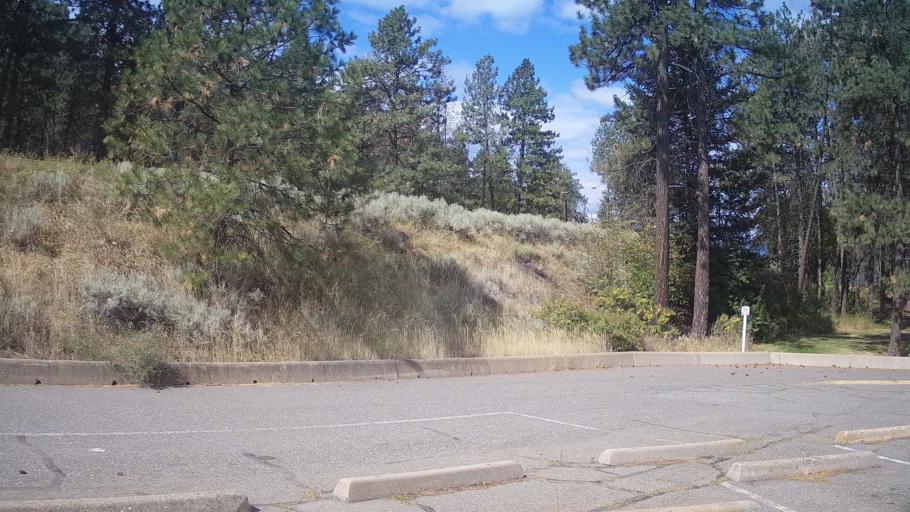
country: CA
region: British Columbia
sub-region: Thompson-Nicola Regional District
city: Ashcroft
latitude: 50.2544
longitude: -121.5096
